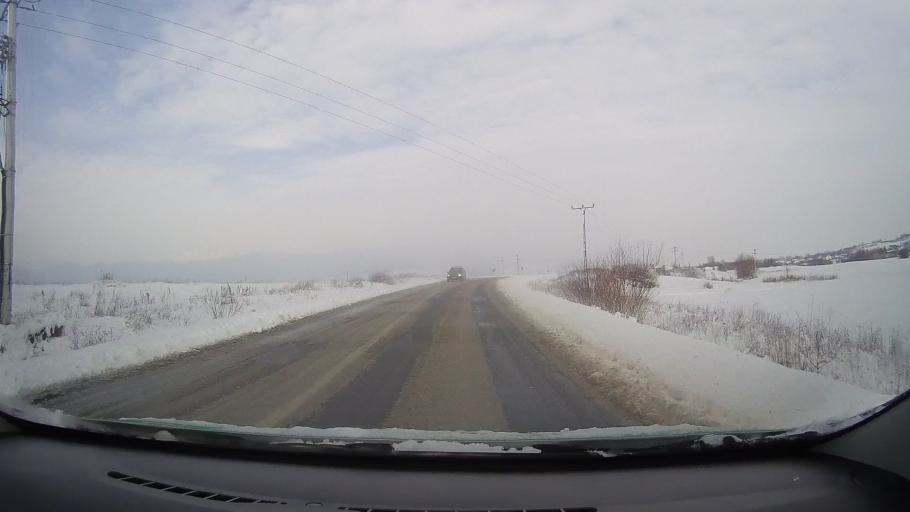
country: RO
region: Alba
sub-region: Comuna Pianu
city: Pianu de Jos
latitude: 45.9682
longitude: 23.4796
